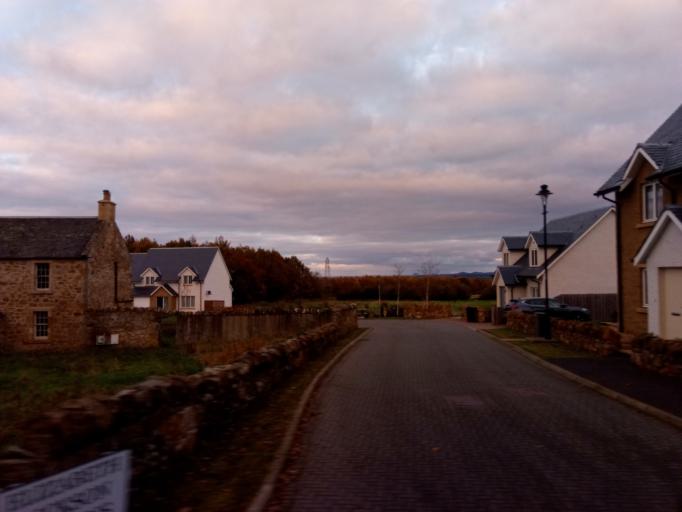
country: GB
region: Scotland
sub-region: Fife
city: Pathhead
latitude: 55.8765
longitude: -3.0052
